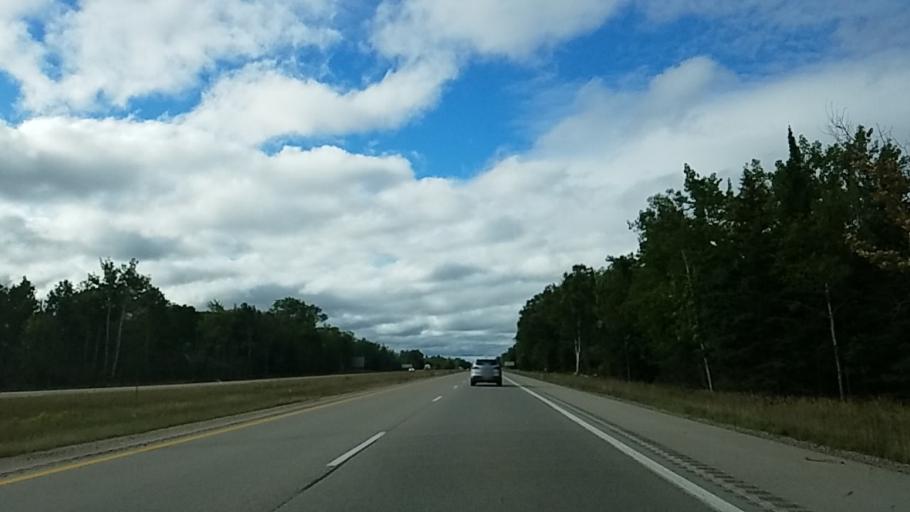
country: US
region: Michigan
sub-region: Mackinac County
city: Saint Ignace
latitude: 45.7487
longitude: -84.7289
